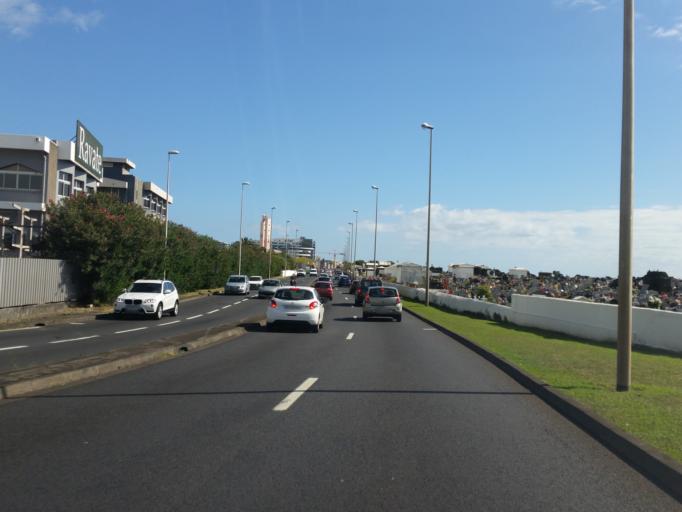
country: RE
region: Reunion
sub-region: Reunion
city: Saint-Denis
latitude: -20.8832
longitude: 55.4653
